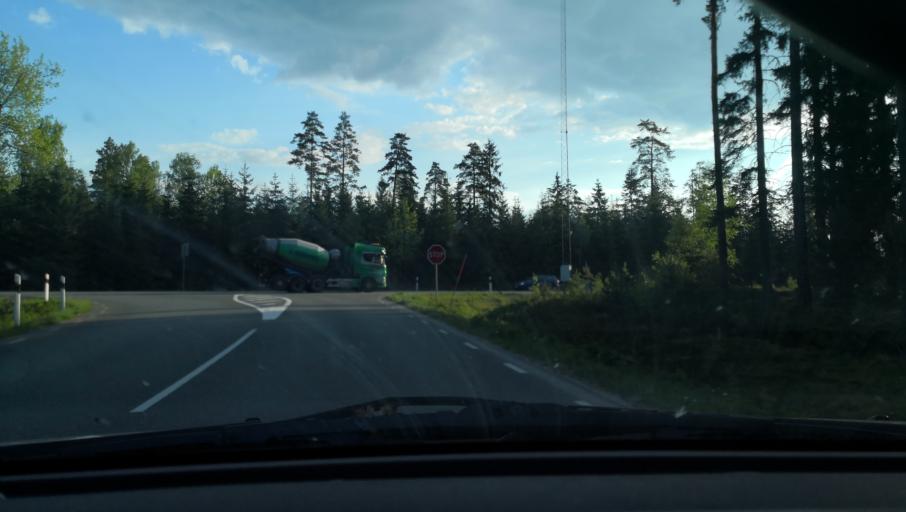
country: SE
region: Joenkoeping
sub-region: Vetlanda Kommun
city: Landsbro
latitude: 57.3938
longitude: 14.8273
